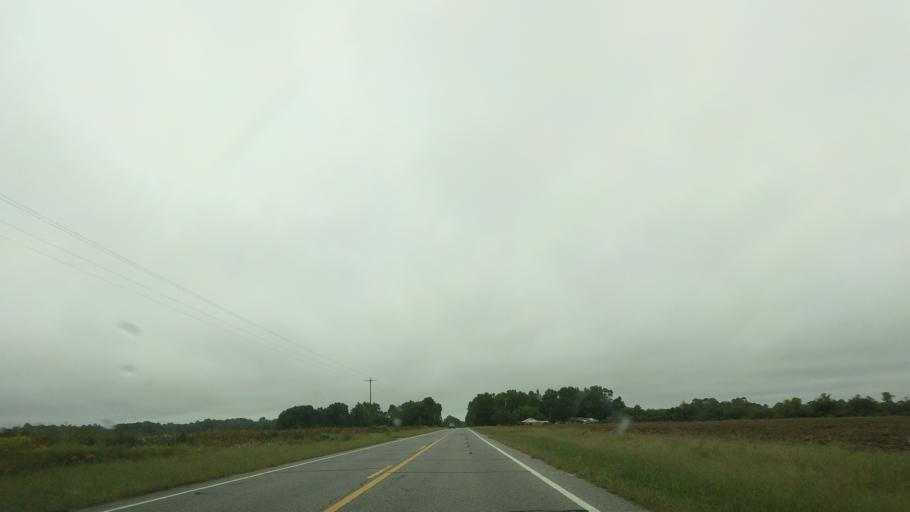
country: US
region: Georgia
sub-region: Berrien County
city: Enigma
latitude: 31.4797
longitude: -83.2379
